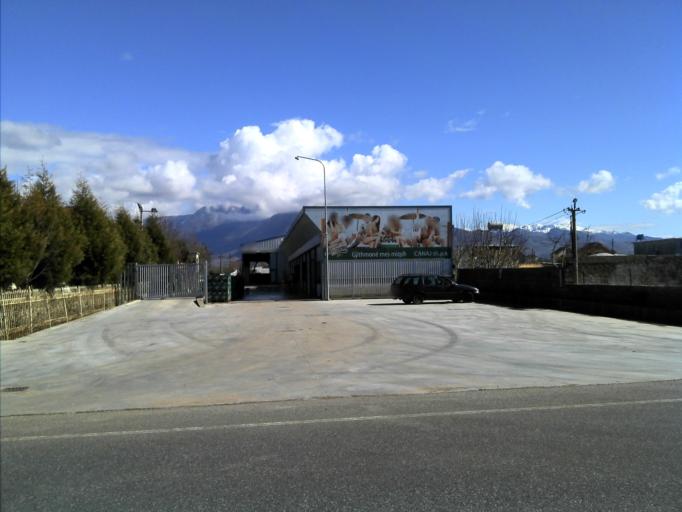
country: AL
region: Shkoder
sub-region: Rrethi i Malesia e Madhe
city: Grude-Fushe
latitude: 42.1571
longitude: 19.4729
